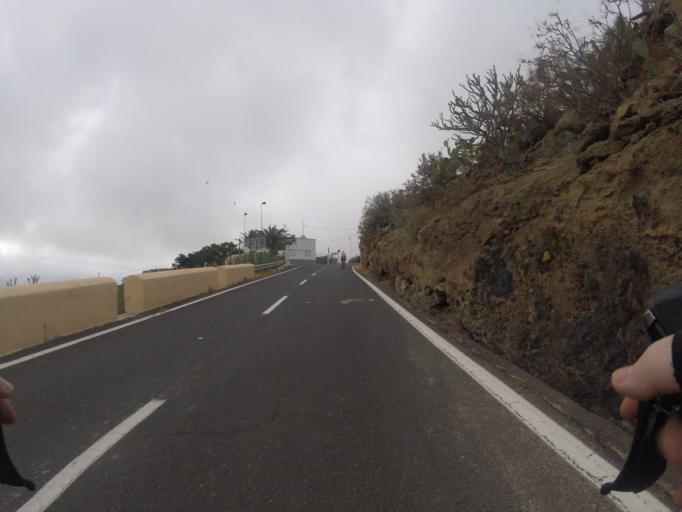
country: ES
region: Canary Islands
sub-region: Provincia de Santa Cruz de Tenerife
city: Fasnia
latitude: 28.2205
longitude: -16.4497
